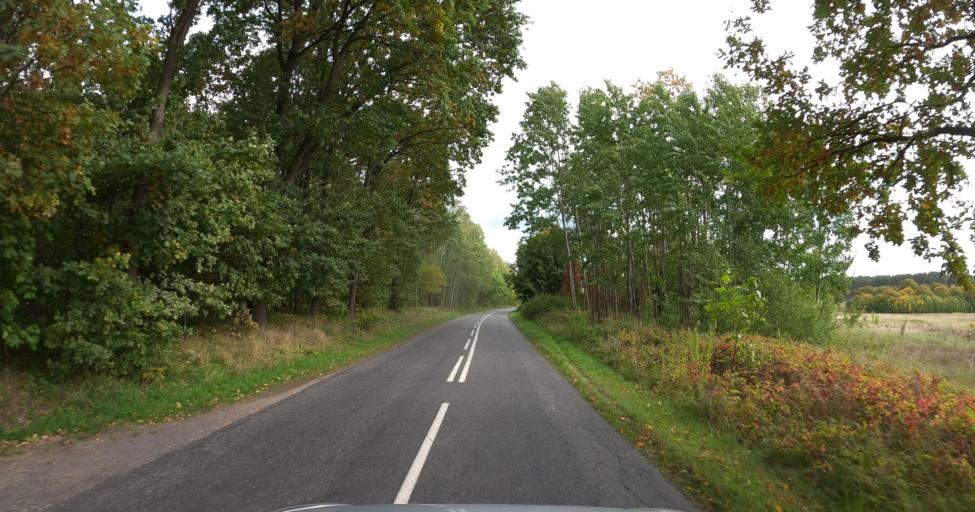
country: PL
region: Lubusz
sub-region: Powiat zielonogorski
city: Zabor
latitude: 51.9469
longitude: 15.6673
